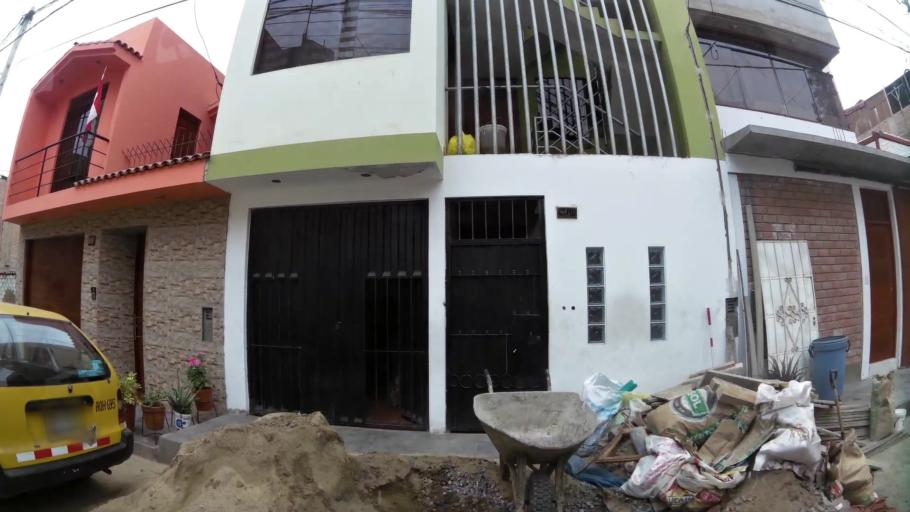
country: PE
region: Lima
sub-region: Lima
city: Surco
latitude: -12.1834
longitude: -77.0126
